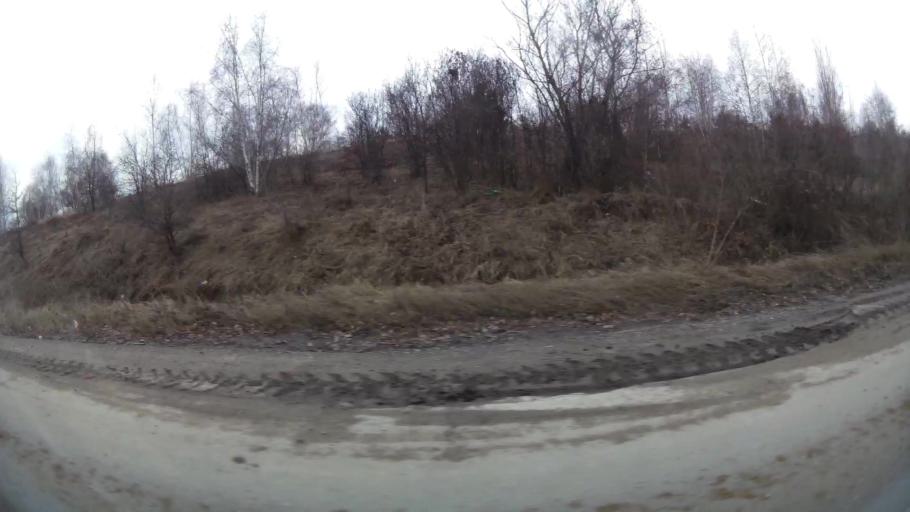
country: BG
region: Sofiya
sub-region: Obshtina Bozhurishte
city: Bozhurishte
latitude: 42.7096
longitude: 23.2303
